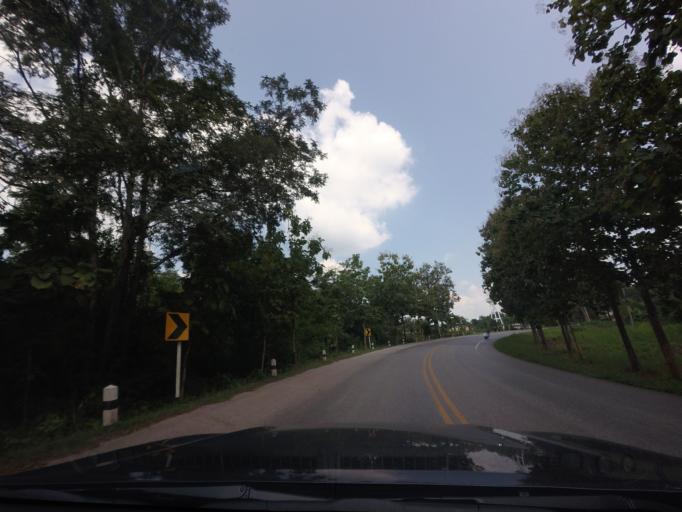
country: TH
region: Phitsanulok
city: Chat Trakan
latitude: 17.2826
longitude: 100.5342
